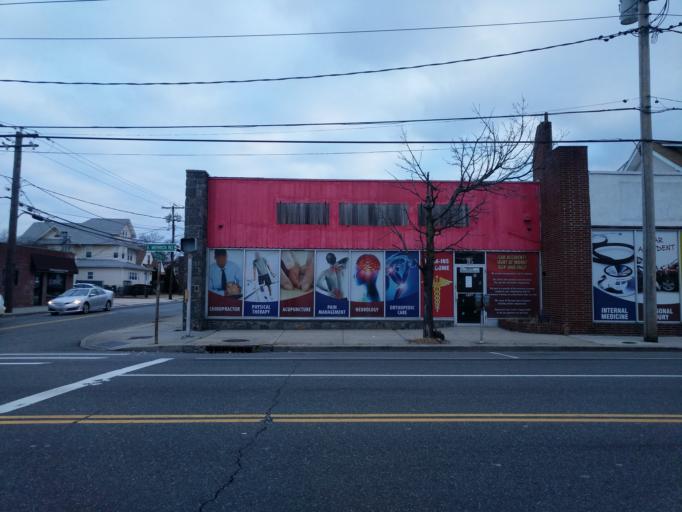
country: US
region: New York
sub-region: Nassau County
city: Valley Stream
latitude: 40.6639
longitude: -73.6949
